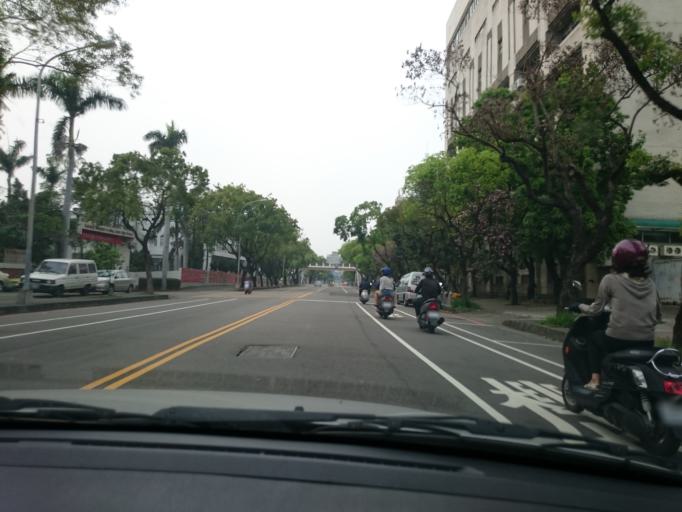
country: TW
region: Taiwan
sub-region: Taichung City
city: Taichung
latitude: 24.1562
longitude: 120.6344
